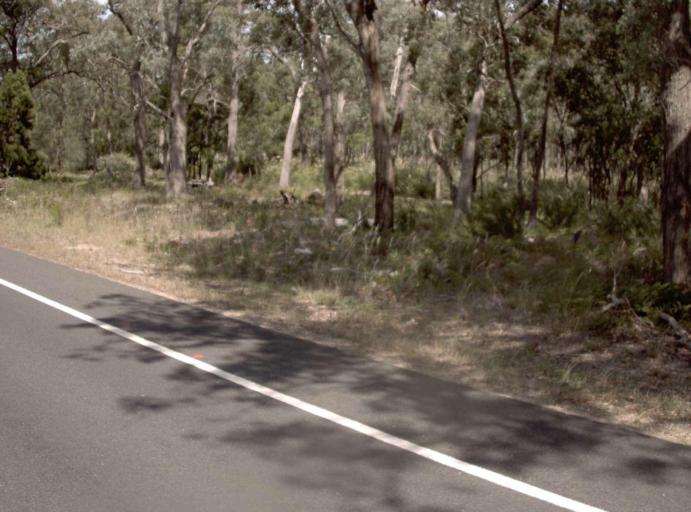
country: AU
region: Victoria
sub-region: Wellington
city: Sale
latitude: -37.9201
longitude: 147.2576
